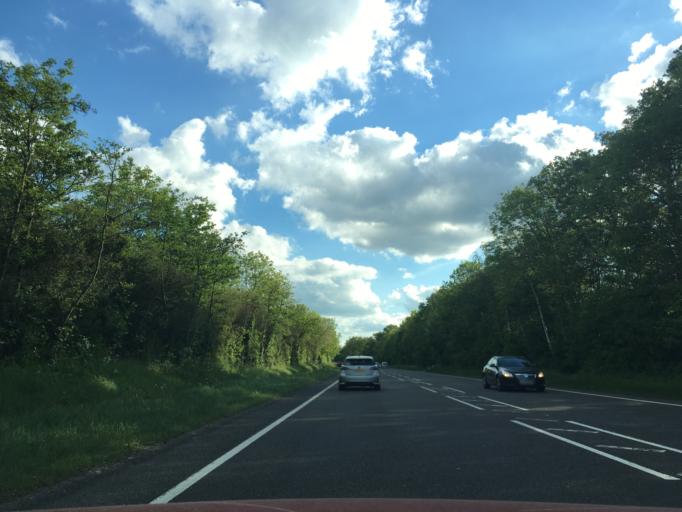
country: GB
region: England
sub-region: Warwickshire
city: Stratford-upon-Avon
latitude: 52.2235
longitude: -1.7051
